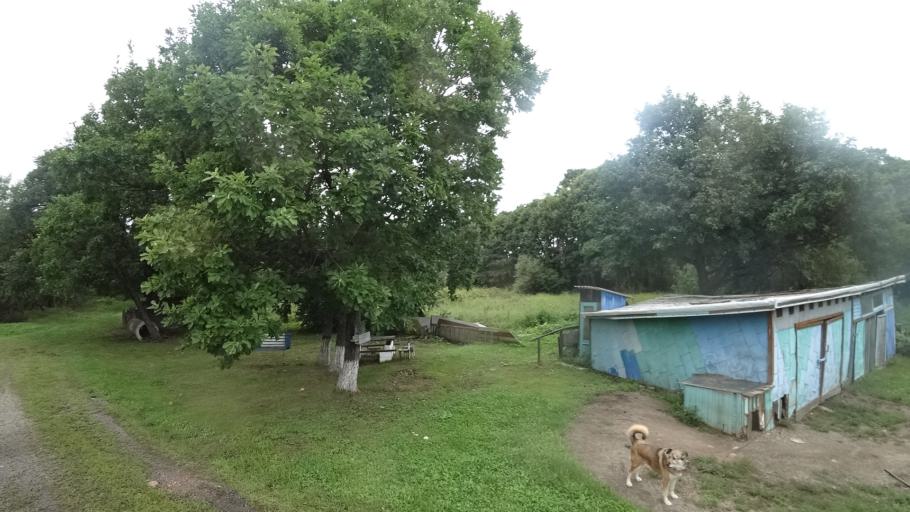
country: RU
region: Primorskiy
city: Monastyrishche
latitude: 44.2680
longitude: 132.4546
